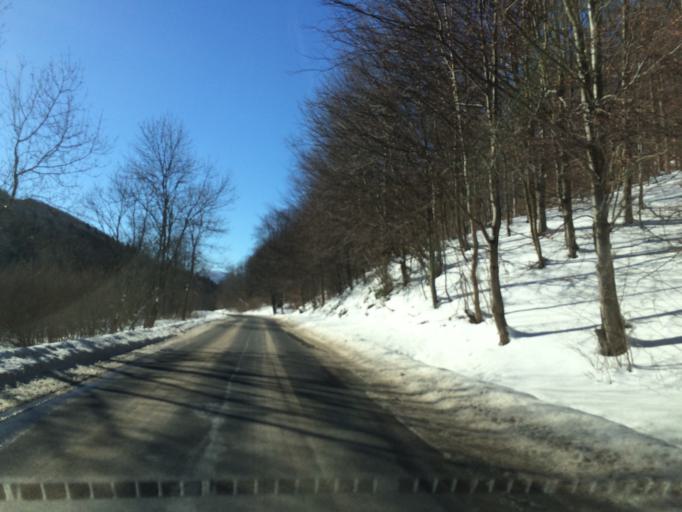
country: PL
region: Subcarpathian Voivodeship
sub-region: Powiat bieszczadzki
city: Lutowiska
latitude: 49.1233
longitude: 22.6678
